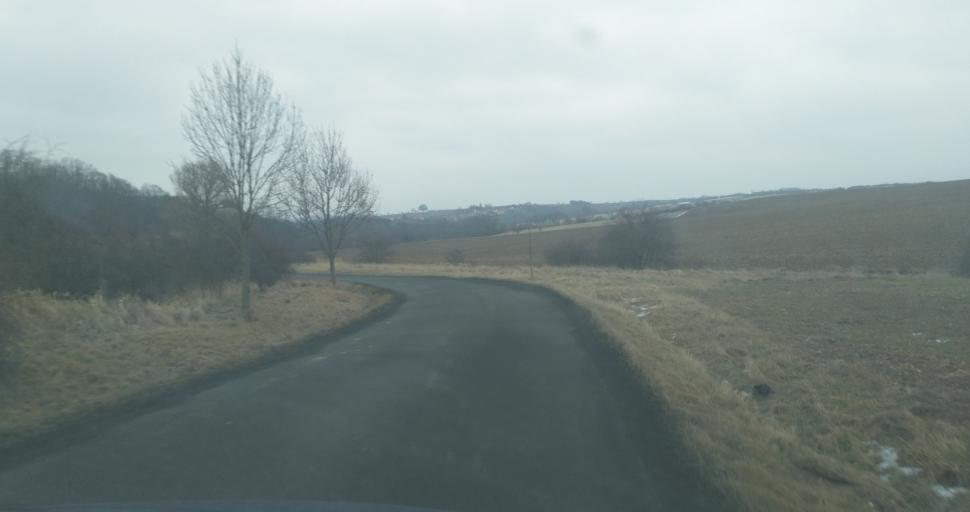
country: CZ
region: Central Bohemia
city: Zebrak
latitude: 49.8826
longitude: 13.9378
